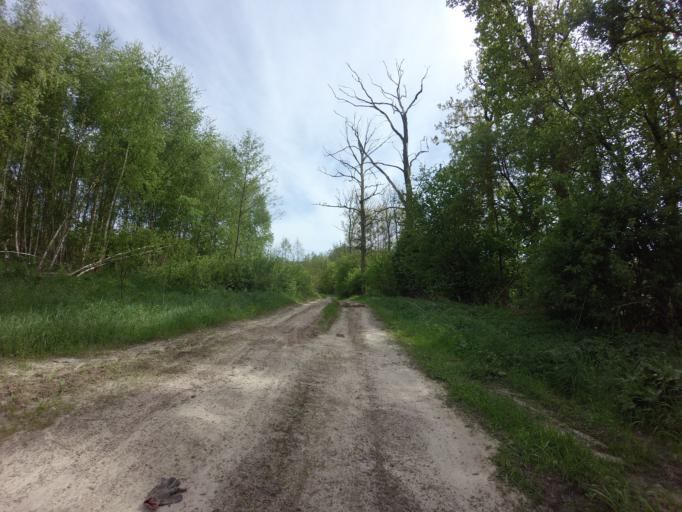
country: PL
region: West Pomeranian Voivodeship
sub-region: Powiat choszczenski
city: Recz
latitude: 53.1567
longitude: 15.6180
